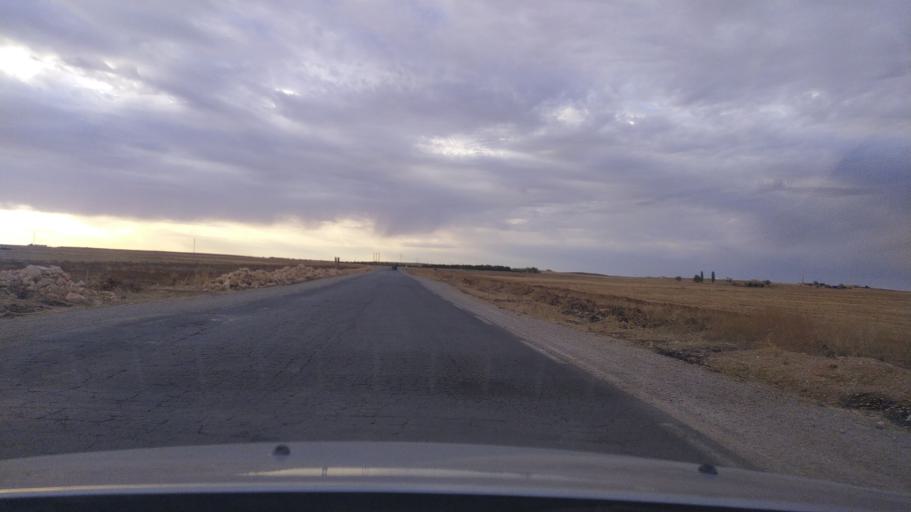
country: DZ
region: Tiaret
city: Frenda
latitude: 34.9805
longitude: 1.1485
